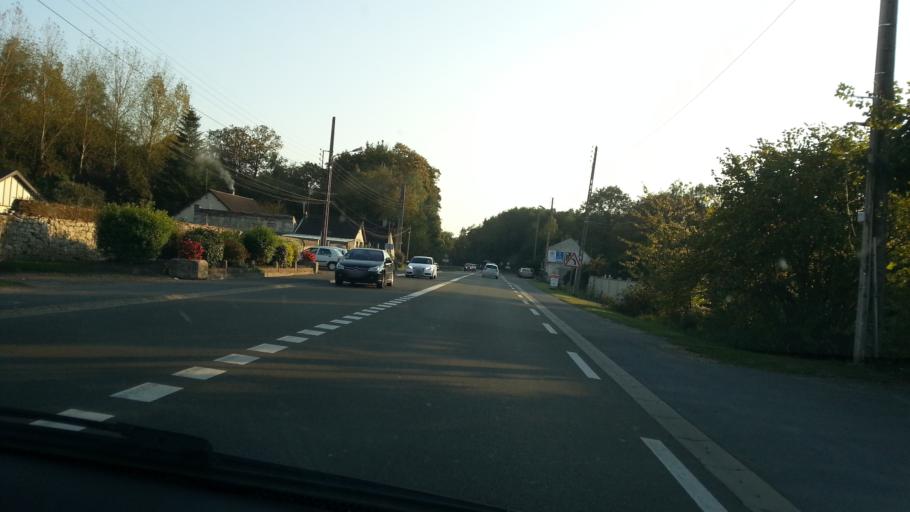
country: FR
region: Picardie
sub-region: Departement de l'Oise
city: Saint-Martin-Longueau
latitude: 49.3346
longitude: 2.6038
